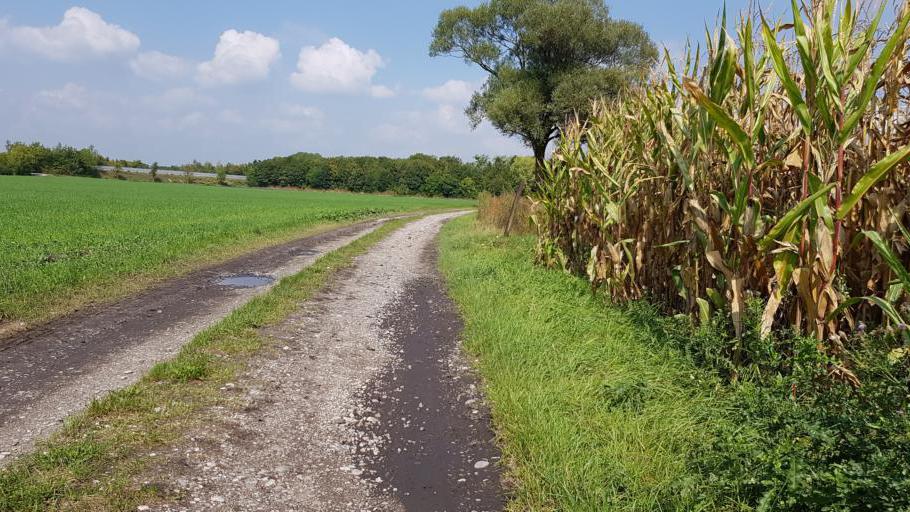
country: DE
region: Bavaria
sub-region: Upper Bavaria
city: Karlsfeld
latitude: 48.2111
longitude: 11.5023
